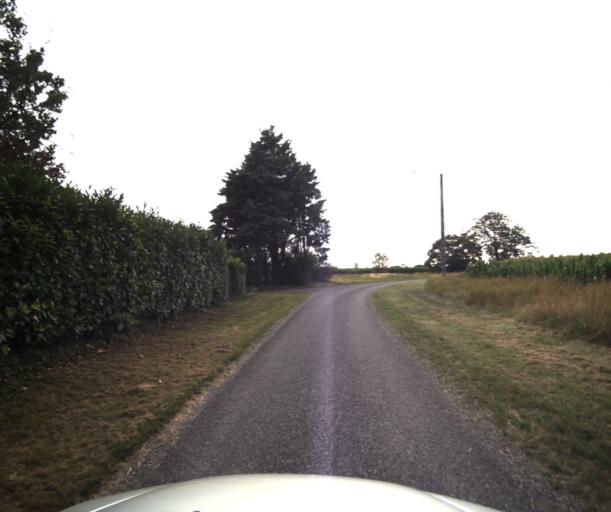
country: FR
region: Midi-Pyrenees
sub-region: Departement de la Haute-Garonne
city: Le Fauga
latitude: 43.4249
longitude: 1.3137
